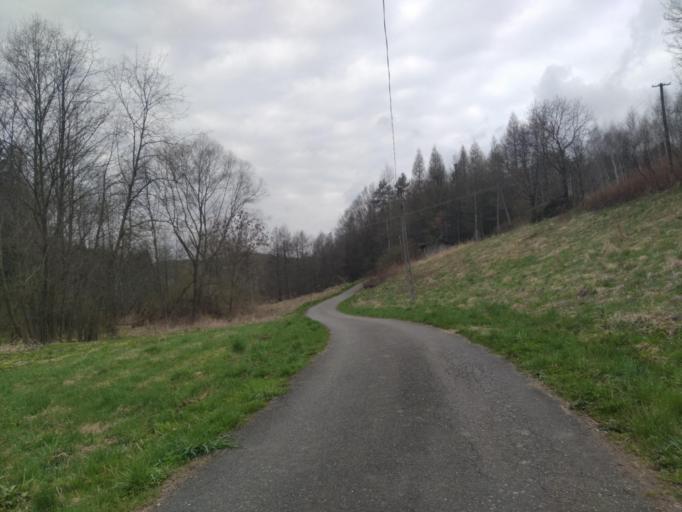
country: PL
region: Subcarpathian Voivodeship
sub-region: Powiat strzyzowski
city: Wysoka Strzyzowska
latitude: 49.8859
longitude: 21.7219
